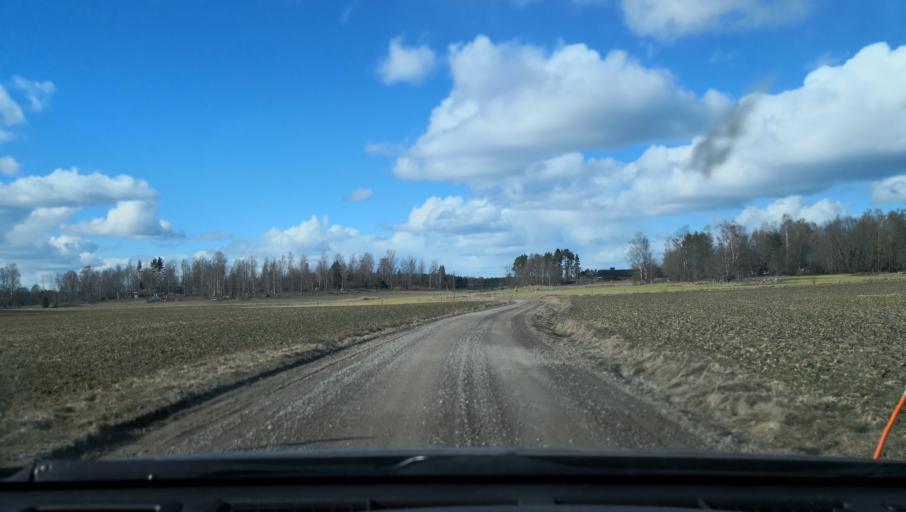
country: SE
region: OErebro
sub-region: Lindesbergs Kommun
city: Fellingsbro
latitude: 59.4214
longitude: 15.6295
